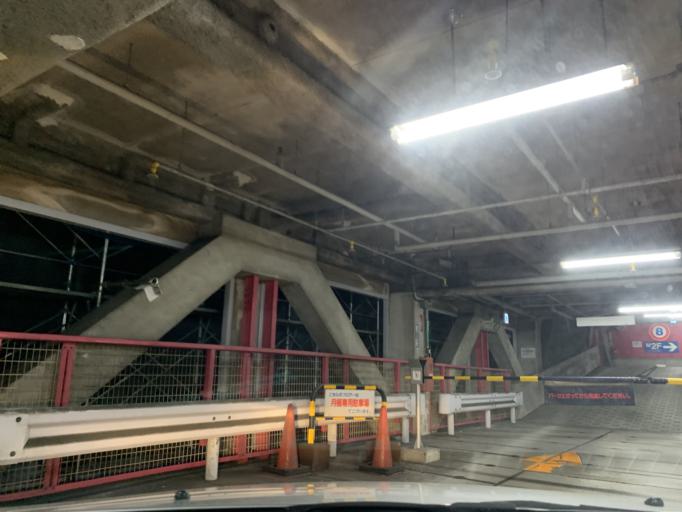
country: JP
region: Tokyo
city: Urayasu
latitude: 35.6484
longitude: 139.9124
